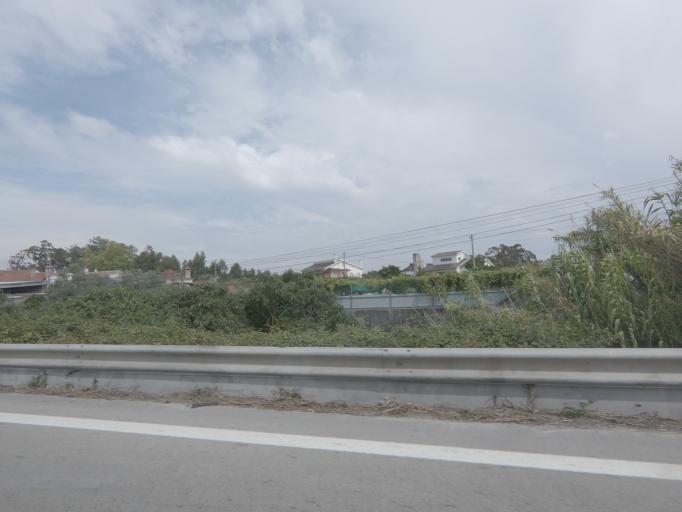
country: PT
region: Leiria
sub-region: Leiria
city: Caranguejeira
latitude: 39.8200
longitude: -8.7275
